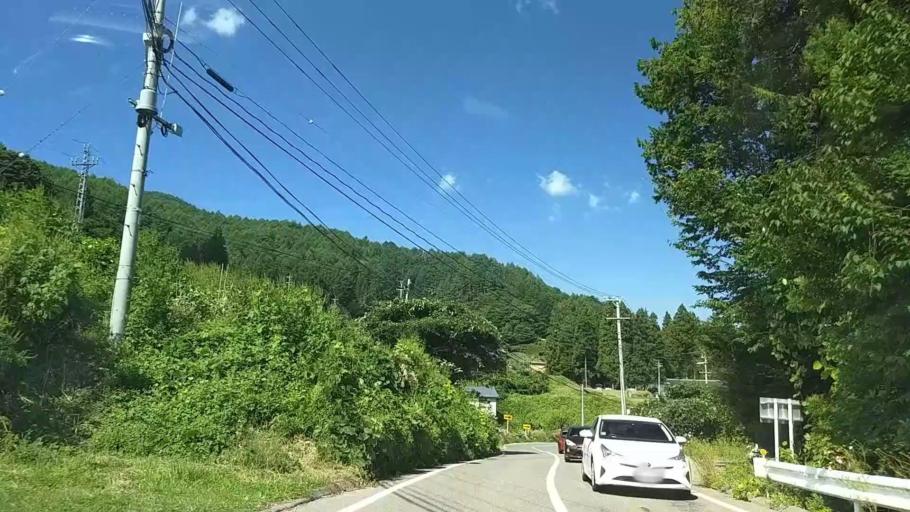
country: JP
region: Nagano
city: Matsumoto
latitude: 36.2048
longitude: 138.0599
